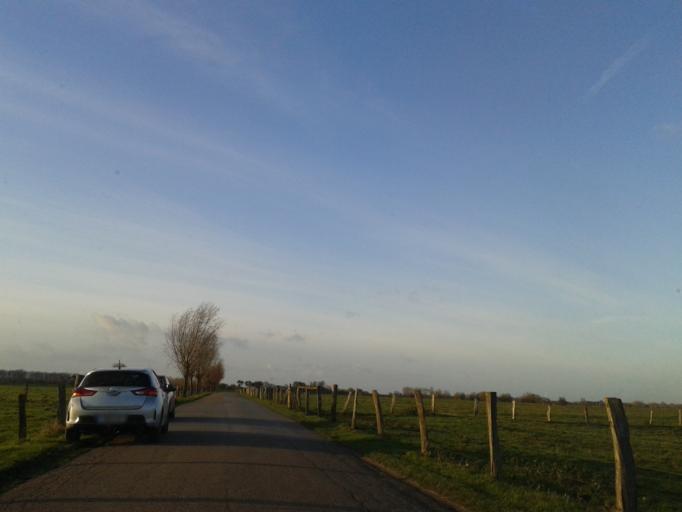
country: DE
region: North Rhine-Westphalia
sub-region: Regierungsbezirk Dusseldorf
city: Xanten
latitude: 51.6510
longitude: 6.5116
